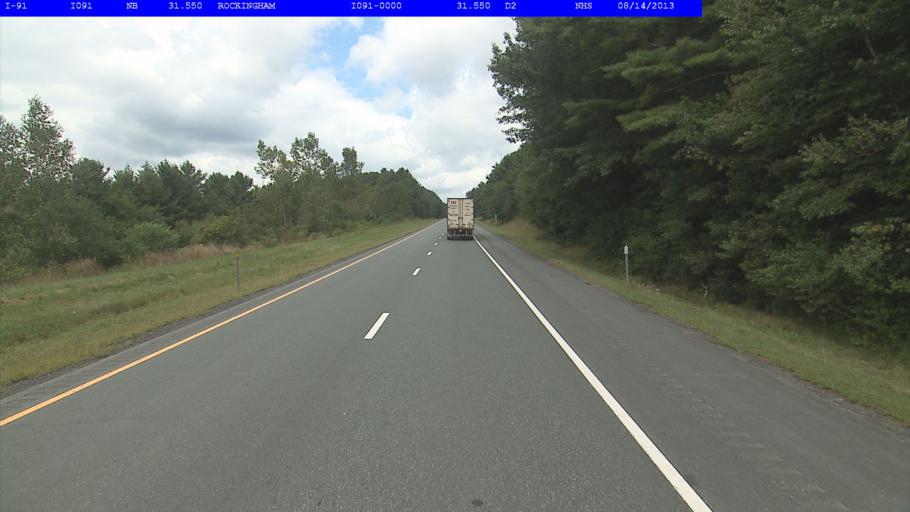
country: US
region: Vermont
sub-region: Windham County
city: Bellows Falls
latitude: 43.1292
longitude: -72.4729
